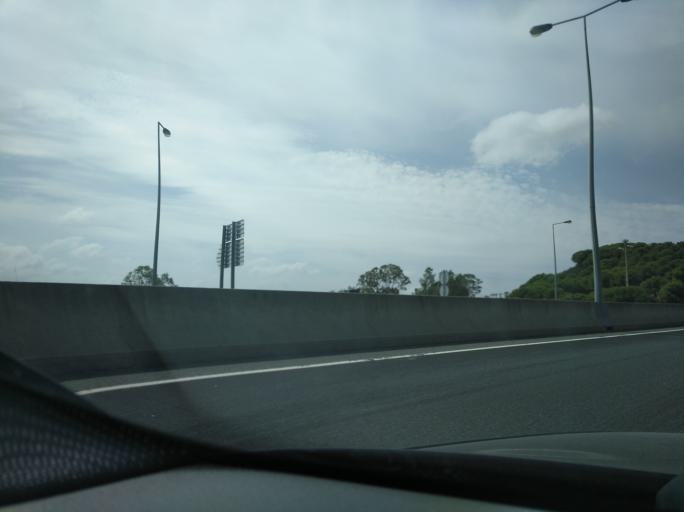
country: PT
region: Faro
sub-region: Castro Marim
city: Castro Marim
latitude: 37.3356
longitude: -7.4959
